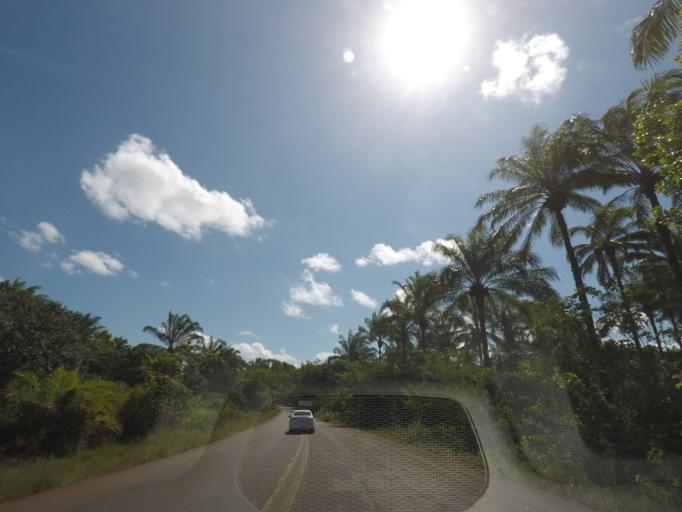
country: BR
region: Bahia
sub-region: Itubera
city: Itubera
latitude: -13.6649
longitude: -39.1188
